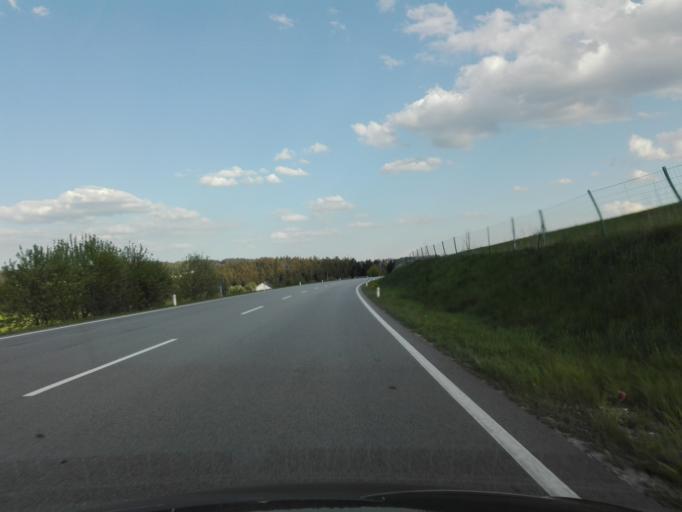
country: AT
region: Upper Austria
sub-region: Politischer Bezirk Rohrbach
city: Kleinzell im Muehlkreis
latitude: 48.4685
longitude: 14.0137
